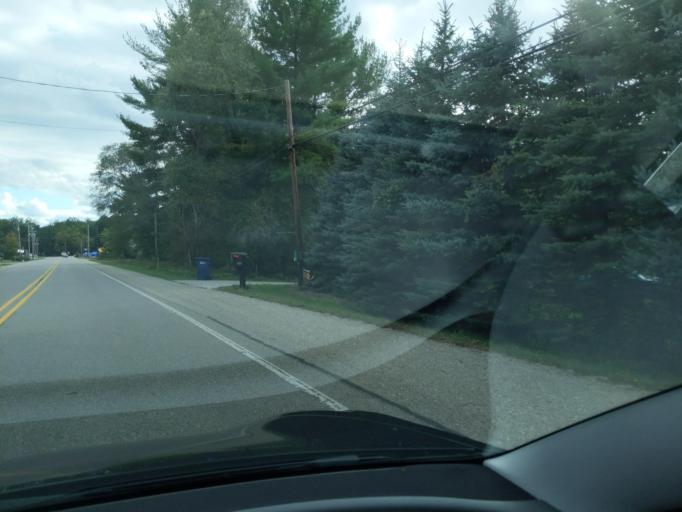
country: US
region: Michigan
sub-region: Kalkaska County
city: Rapid City
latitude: 44.8626
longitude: -85.2817
